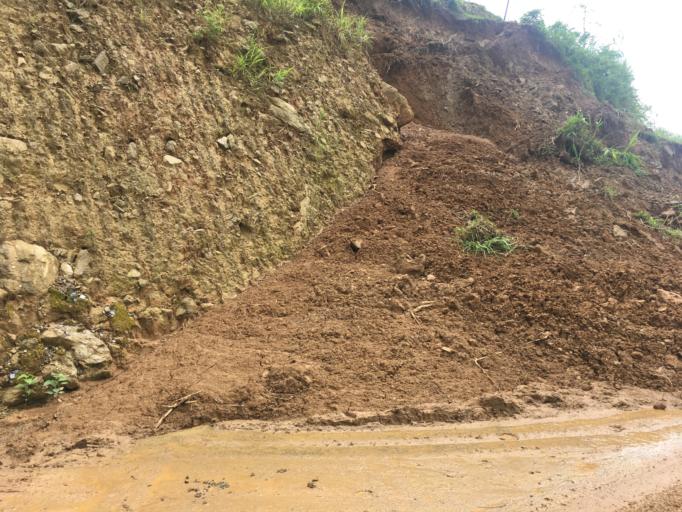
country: VN
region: Ha Giang
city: Thi Tran Tam Son
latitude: 22.9934
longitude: 105.0755
